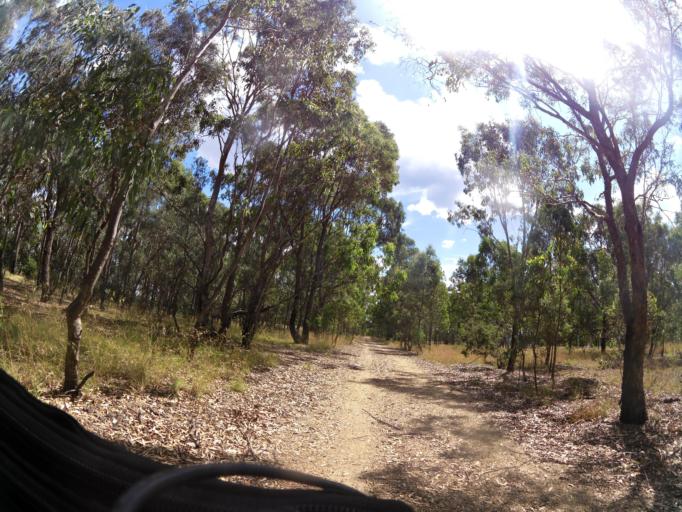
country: AU
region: Victoria
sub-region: Wellington
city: Heyfield
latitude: -37.9832
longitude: 146.7262
